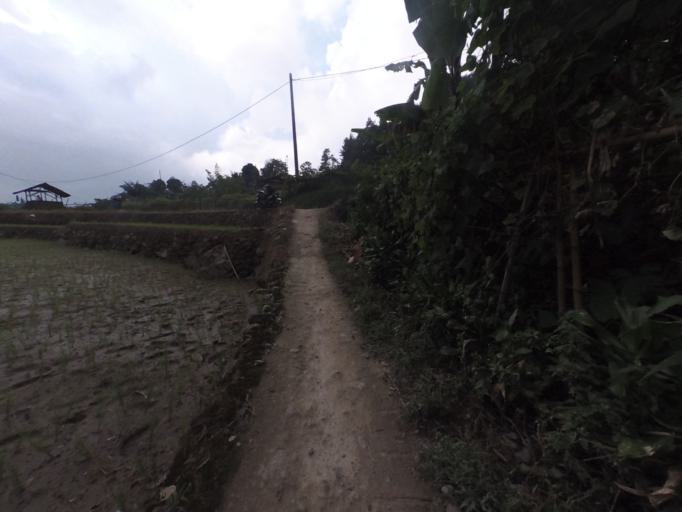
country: ID
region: West Java
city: Cicurug
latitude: -6.7060
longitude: 106.6641
